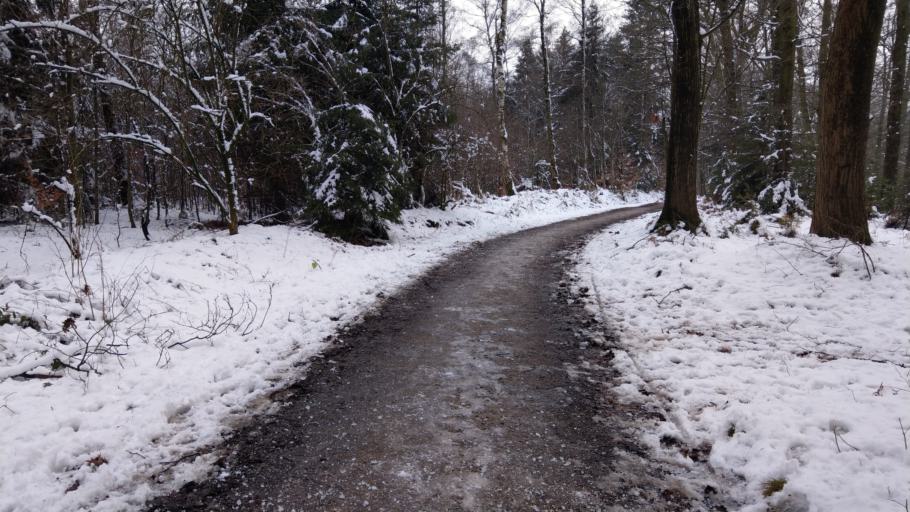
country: BE
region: Wallonia
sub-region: Province de Liege
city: Raeren
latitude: 50.7154
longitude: 6.0986
